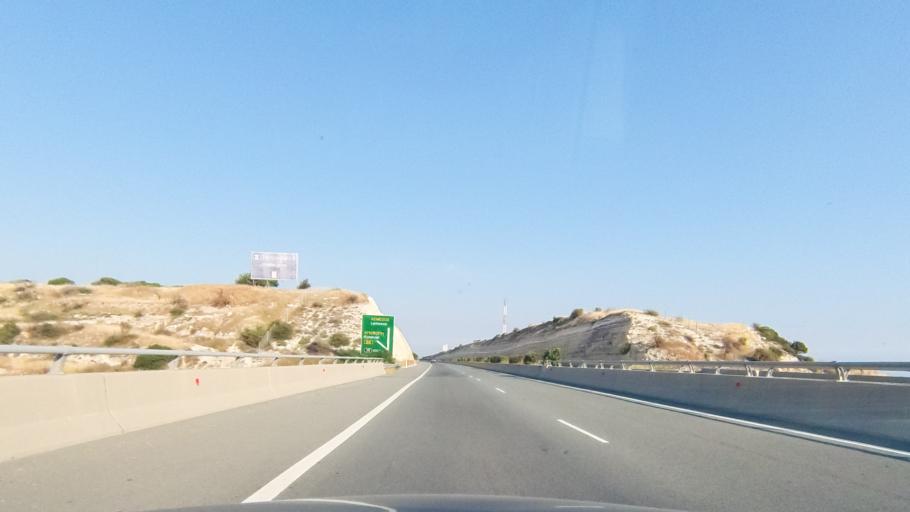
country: CY
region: Limassol
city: Sotira
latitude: 34.6874
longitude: 32.8746
